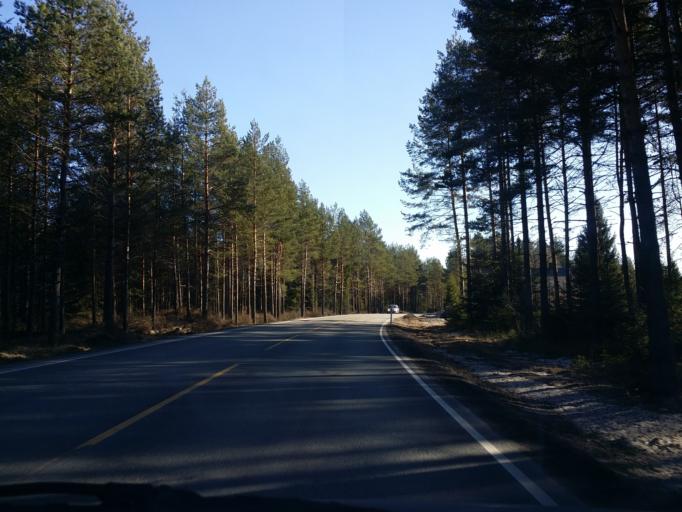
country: NO
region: Buskerud
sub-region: Ringerike
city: Honefoss
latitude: 60.2989
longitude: 10.1777
